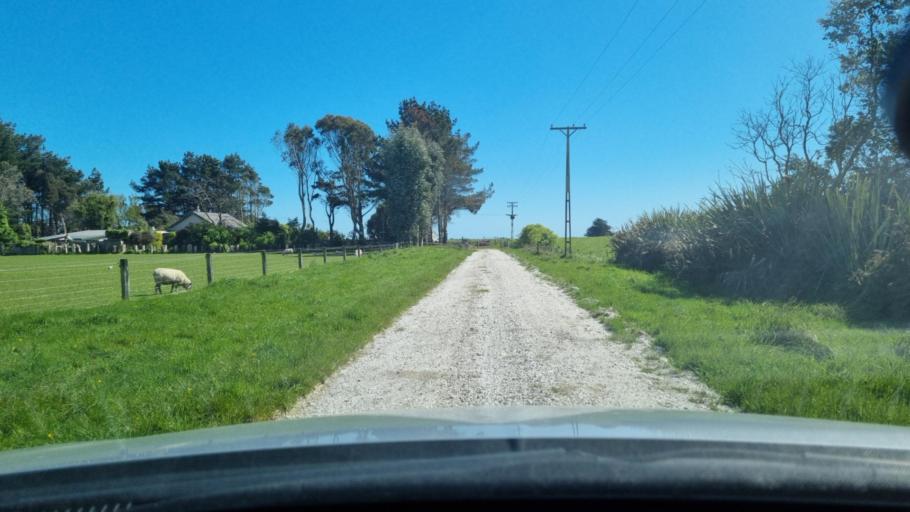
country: NZ
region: Southland
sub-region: Invercargill City
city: Invercargill
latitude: -46.3920
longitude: 168.2929
